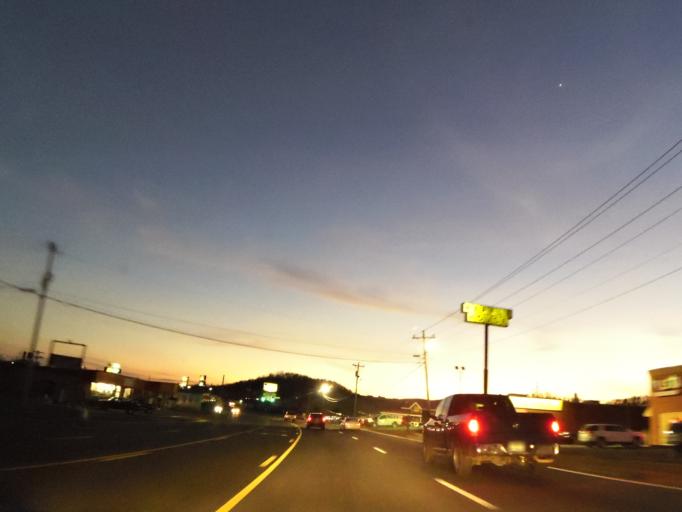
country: US
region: Georgia
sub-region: Whitfield County
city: Dalton
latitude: 34.8016
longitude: -84.9611
